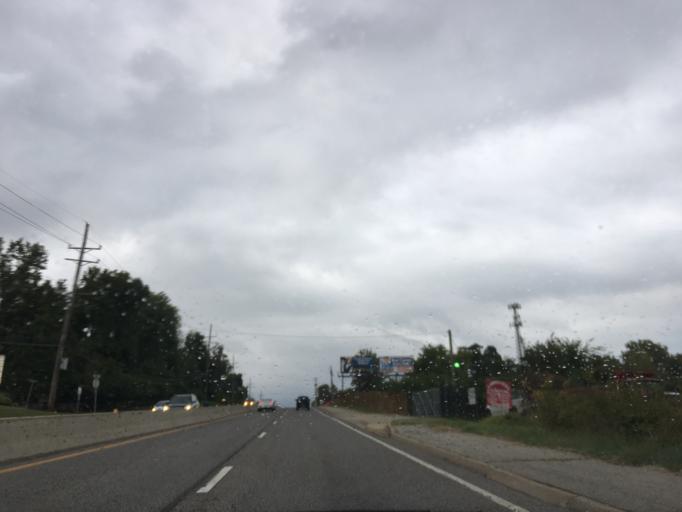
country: US
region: Missouri
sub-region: Saint Louis County
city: Maryland Heights
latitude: 38.7130
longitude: -90.4083
